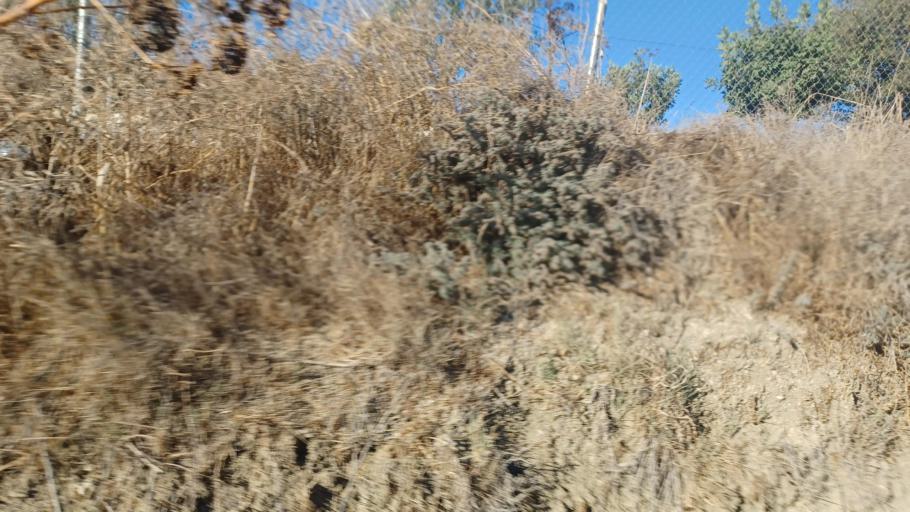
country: CY
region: Pafos
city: Mesogi
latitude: 34.7924
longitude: 32.4804
